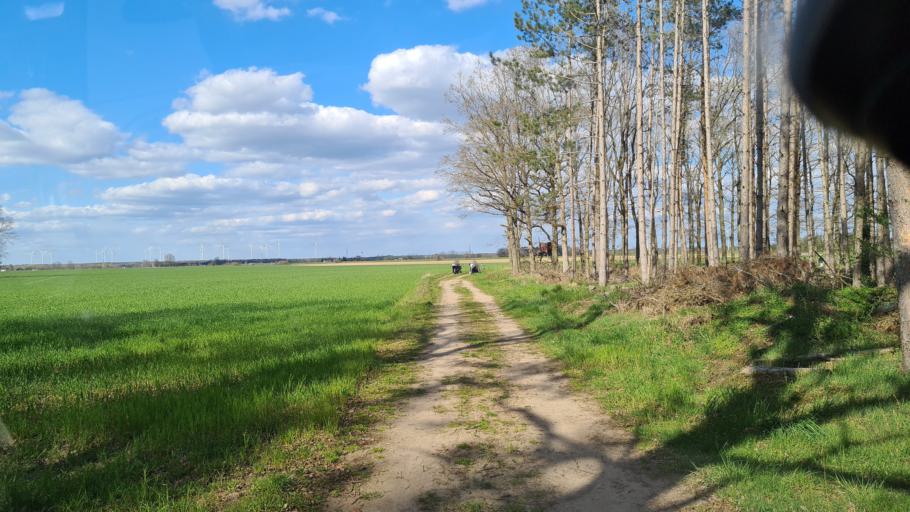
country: DE
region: Brandenburg
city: Falkenberg
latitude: 51.5290
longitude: 13.2863
